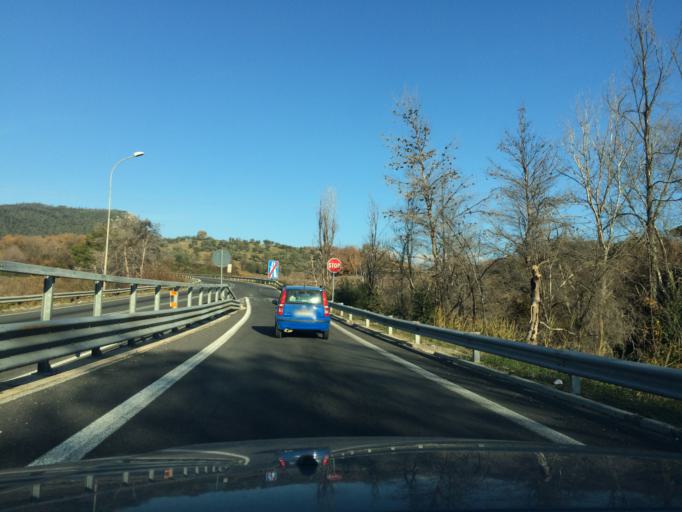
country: IT
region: Umbria
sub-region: Provincia di Terni
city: Fornole
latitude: 42.5315
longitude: 12.4741
